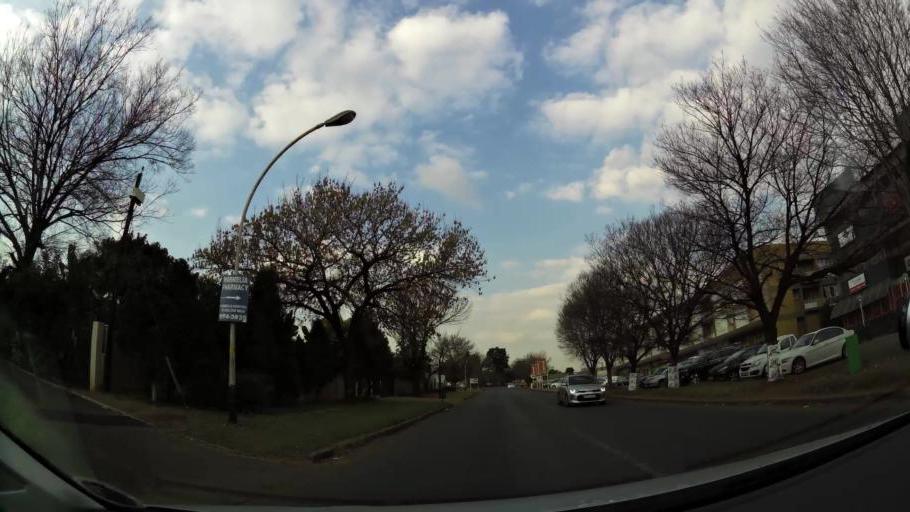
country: ZA
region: Gauteng
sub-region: City of Johannesburg Metropolitan Municipality
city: Modderfontein
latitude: -26.1399
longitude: 28.1878
